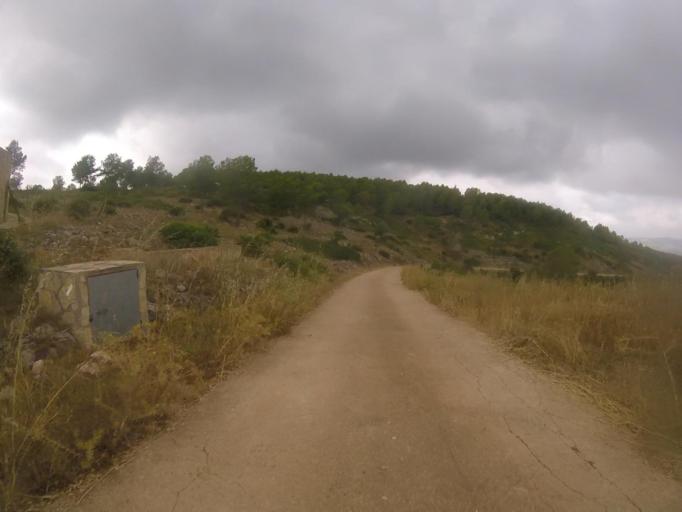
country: ES
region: Valencia
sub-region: Provincia de Castello
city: Santa Magdalena de Pulpis
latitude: 40.3274
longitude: 0.2879
